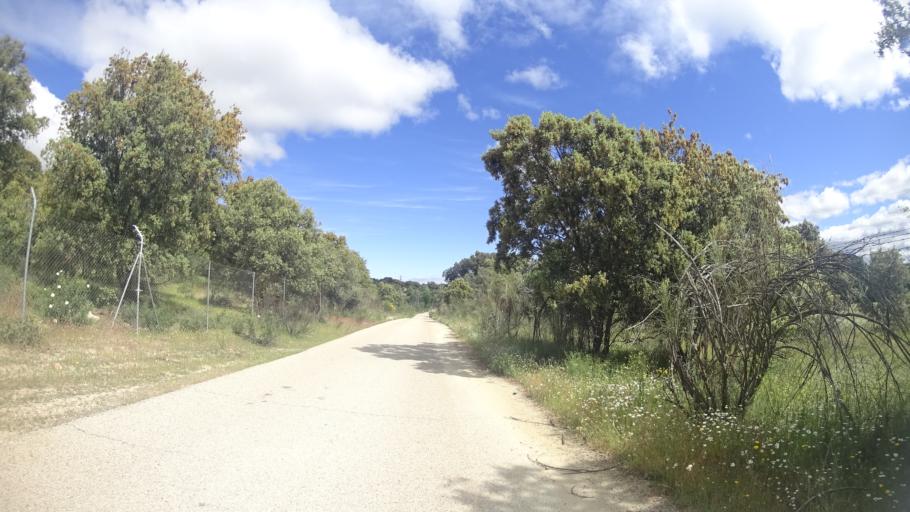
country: ES
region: Madrid
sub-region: Provincia de Madrid
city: Brunete
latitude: 40.4092
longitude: -3.9503
